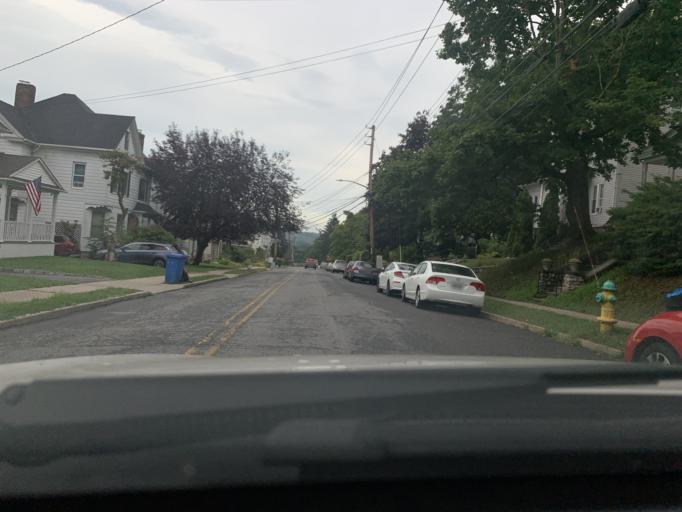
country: US
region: New York
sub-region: Westchester County
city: Ossining
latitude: 41.1630
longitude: -73.8555
